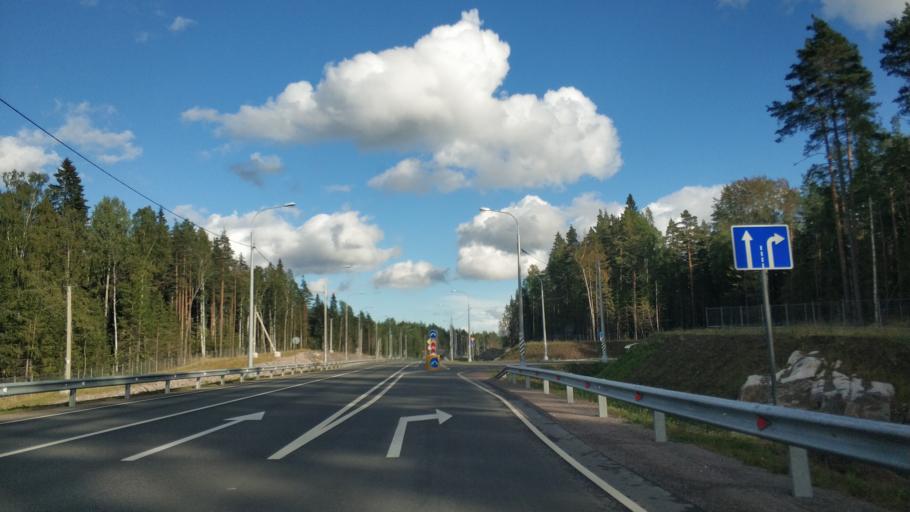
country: RU
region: Leningrad
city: Kuznechnoye
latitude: 61.0948
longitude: 29.9876
